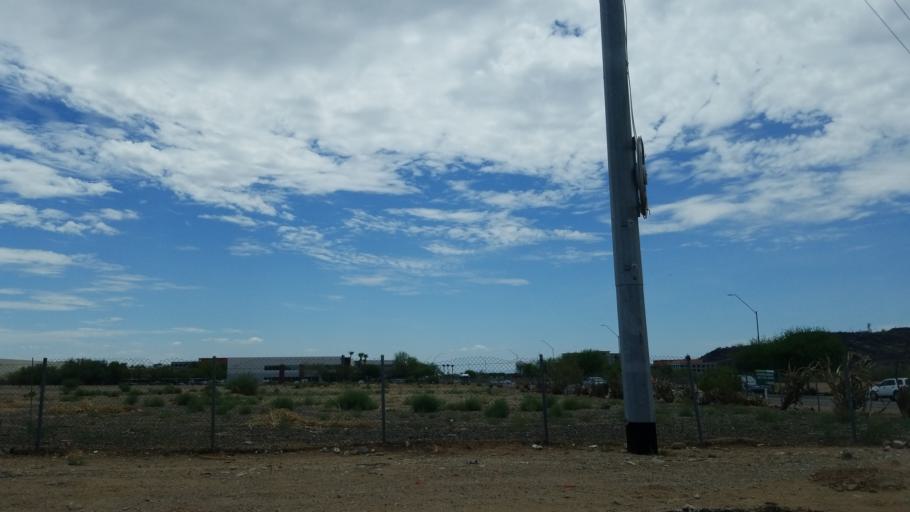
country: US
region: Arizona
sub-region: Maricopa County
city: Anthem
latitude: 33.7056
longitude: -112.1086
